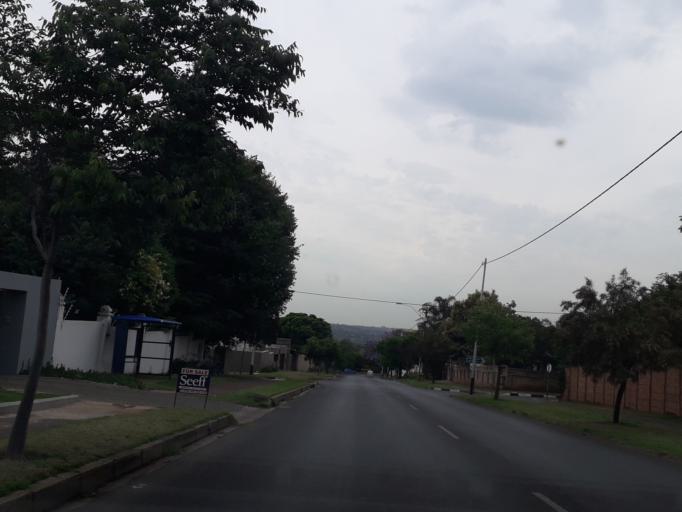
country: ZA
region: Gauteng
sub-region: City of Johannesburg Metropolitan Municipality
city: Johannesburg
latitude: -26.1352
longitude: 27.9858
